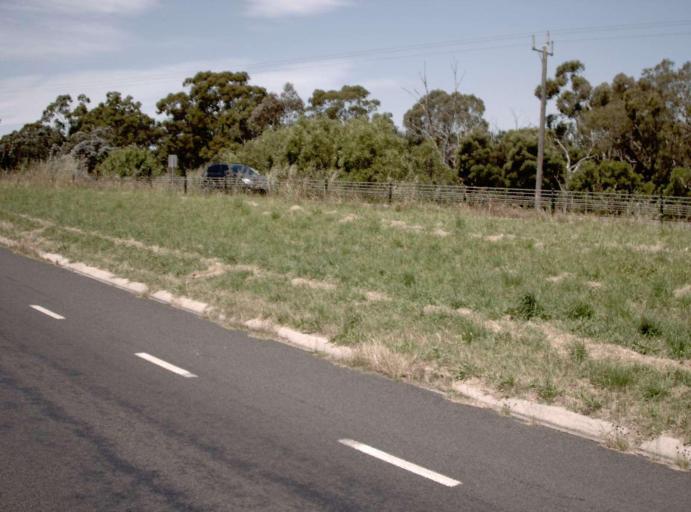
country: AU
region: Victoria
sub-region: Latrobe
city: Traralgon
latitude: -38.2074
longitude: 146.5014
